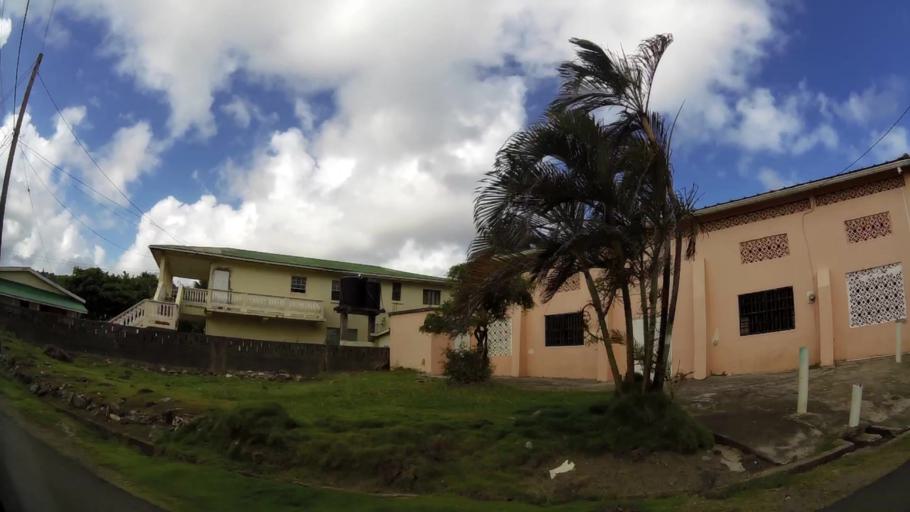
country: LC
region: Dennery Quarter
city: Dennery
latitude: 13.9087
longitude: -60.8914
